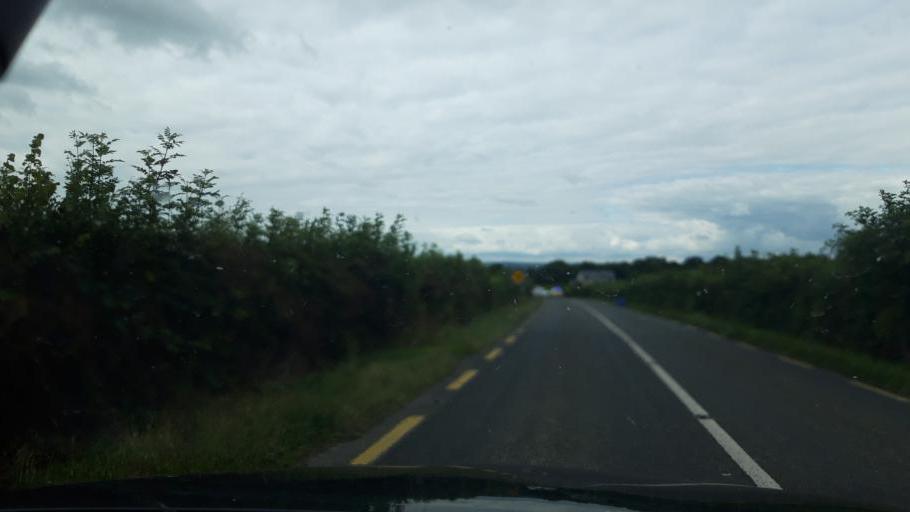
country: IE
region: Leinster
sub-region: Kilkenny
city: Thomastown
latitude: 52.6226
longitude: -7.0701
